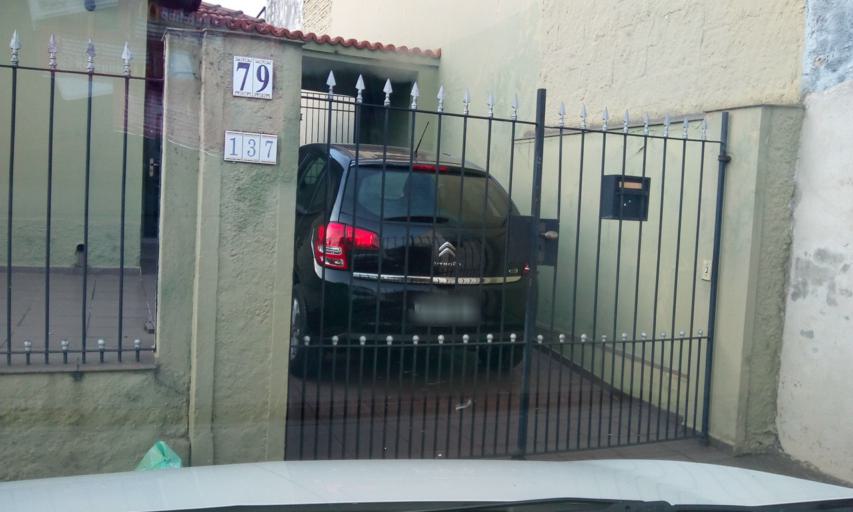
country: BR
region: Sao Paulo
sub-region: Diadema
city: Diadema
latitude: -23.6221
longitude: -46.6514
